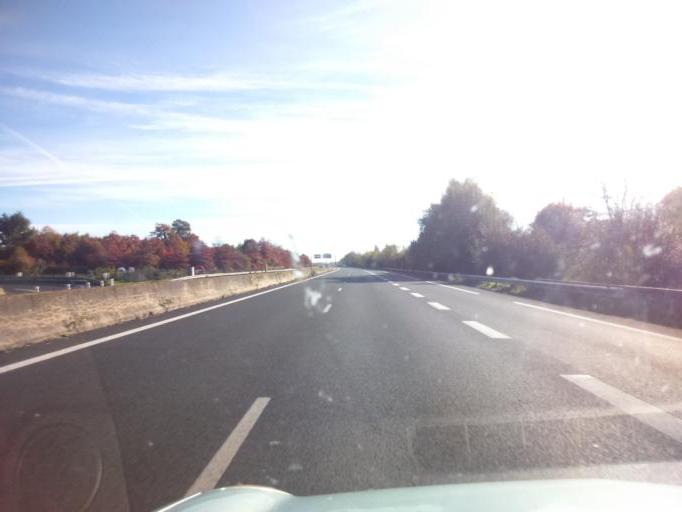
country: FR
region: Poitou-Charentes
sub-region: Departement de la Charente-Maritime
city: Breuil-Magne
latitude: 45.9619
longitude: -0.9581
